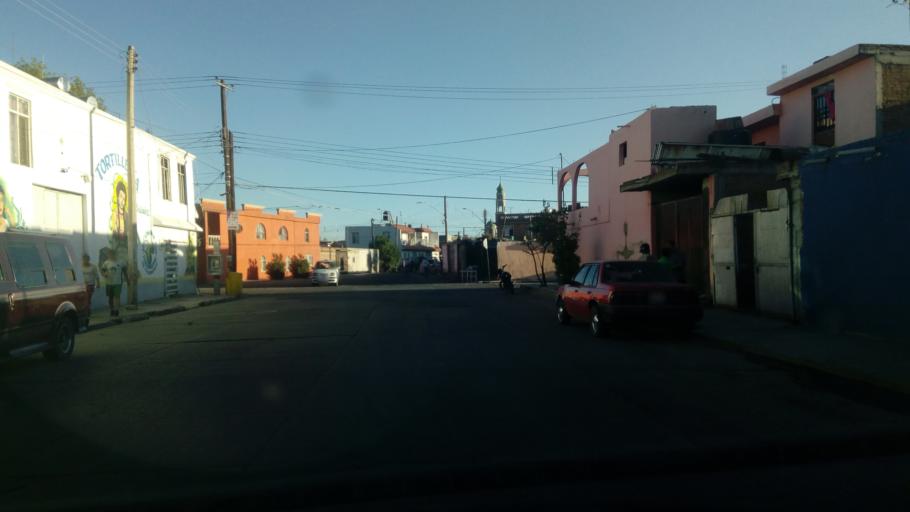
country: MX
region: Durango
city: Victoria de Durango
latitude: 24.0007
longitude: -104.6797
